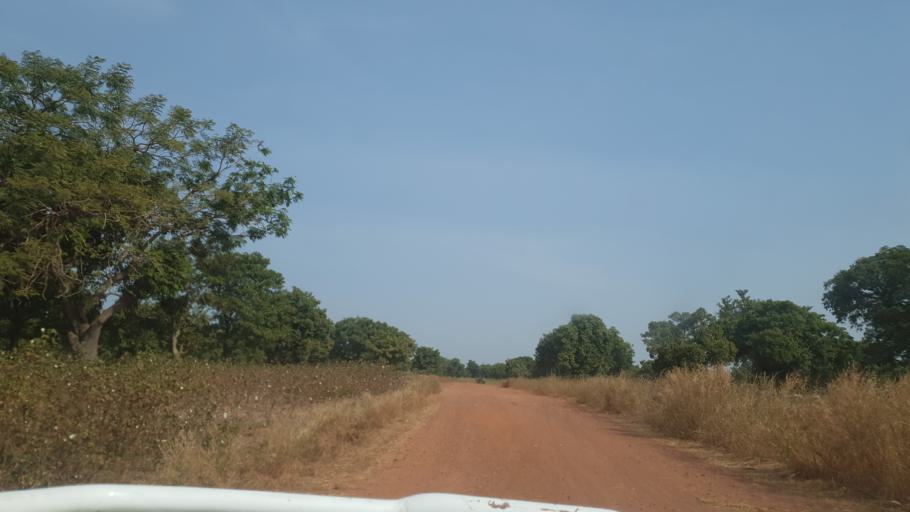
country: ML
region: Koulikoro
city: Dioila
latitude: 12.2283
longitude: -6.2189
